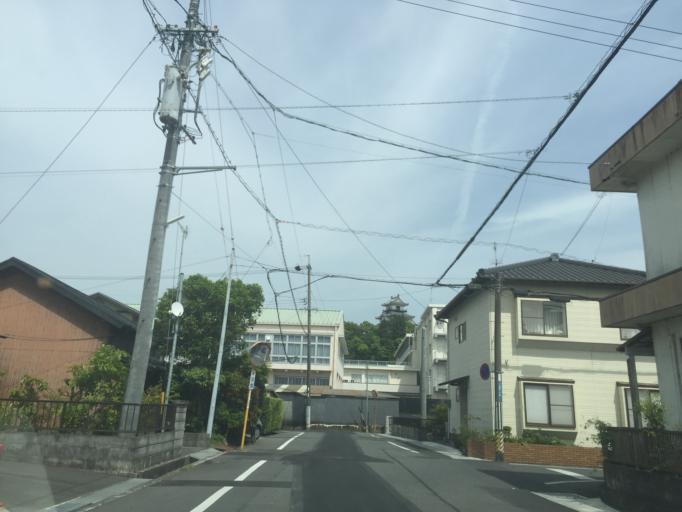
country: JP
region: Shizuoka
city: Kakegawa
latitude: 34.7754
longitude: 138.0113
